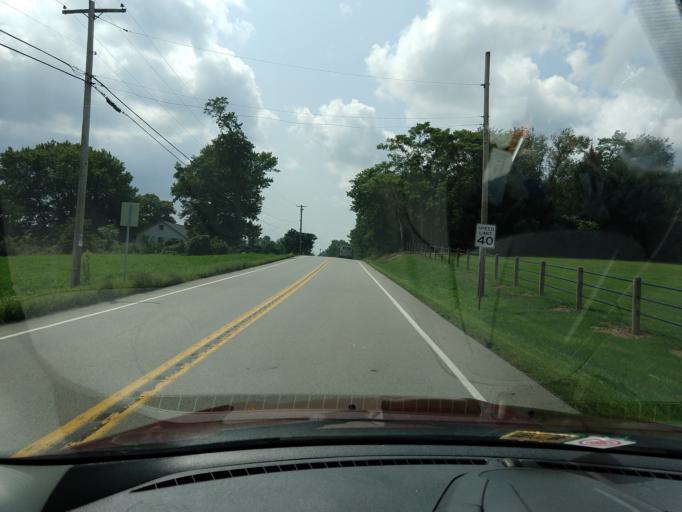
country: US
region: Pennsylvania
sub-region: Washington County
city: McMurray
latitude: 40.1860
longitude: -80.0814
